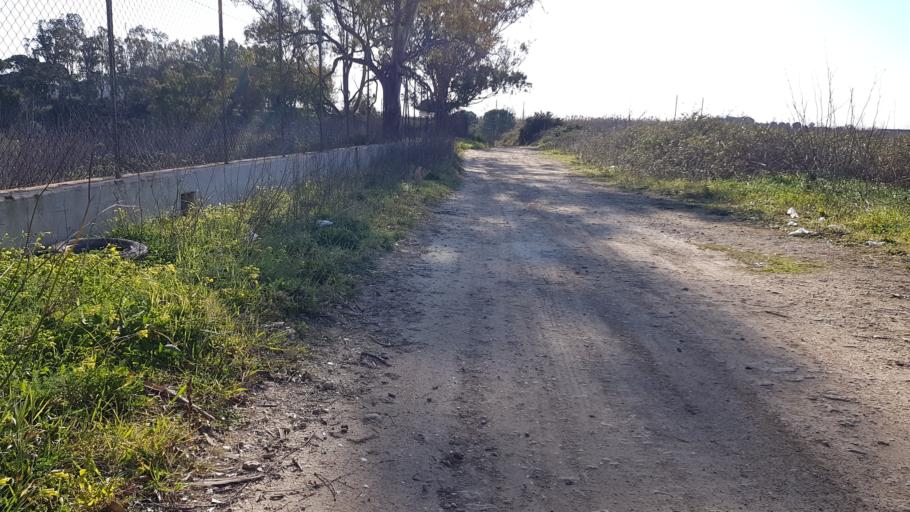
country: IT
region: Apulia
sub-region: Provincia di Brindisi
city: Brindisi
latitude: 40.6262
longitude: 17.8931
